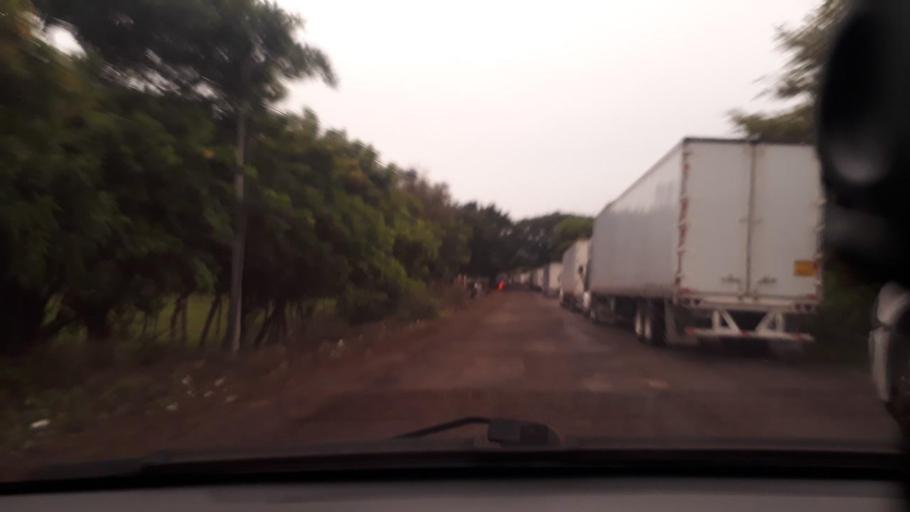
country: GT
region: Jutiapa
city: Atescatempa
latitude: 14.2235
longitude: -89.6973
